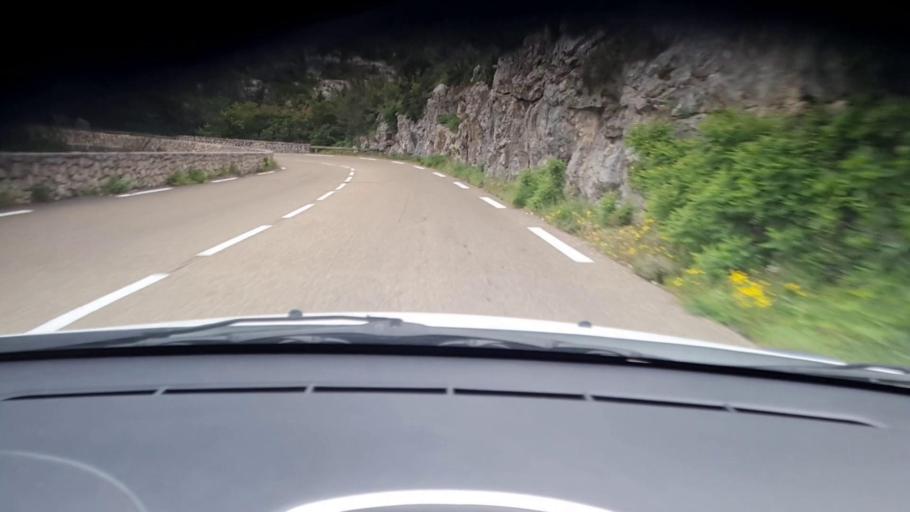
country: FR
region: Languedoc-Roussillon
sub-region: Departement du Gard
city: Blauzac
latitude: 43.9327
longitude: 4.3852
